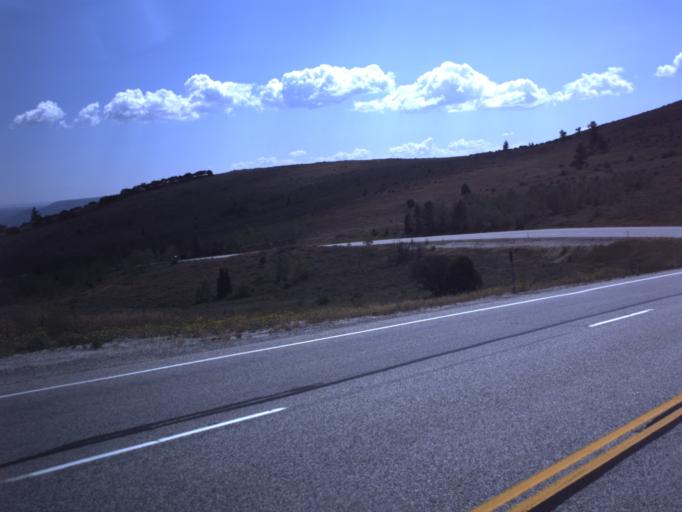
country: US
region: Idaho
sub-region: Bear Lake County
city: Paris
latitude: 41.9302
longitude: -111.4451
